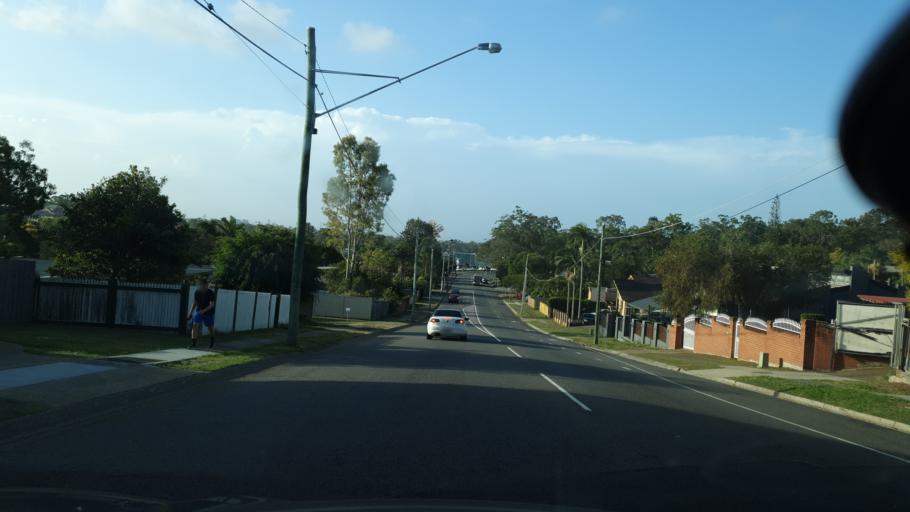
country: AU
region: Queensland
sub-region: Brisbane
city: Belmont
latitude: -27.4879
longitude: 153.1271
